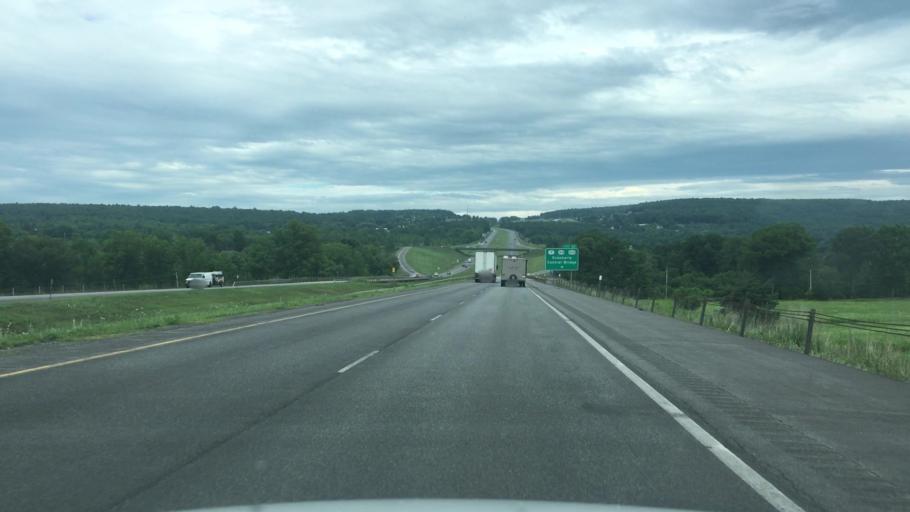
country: US
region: New York
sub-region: Schoharie County
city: Schoharie
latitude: 42.7049
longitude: -74.3257
